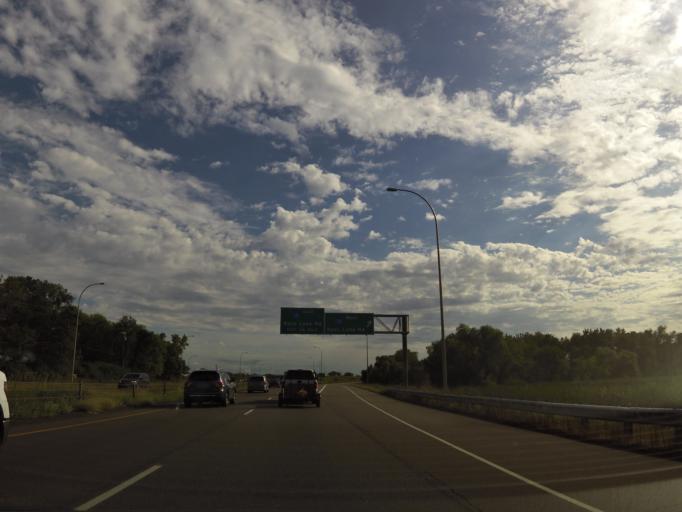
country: US
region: Minnesota
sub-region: Hennepin County
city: New Hope
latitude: 45.0624
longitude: -93.4010
